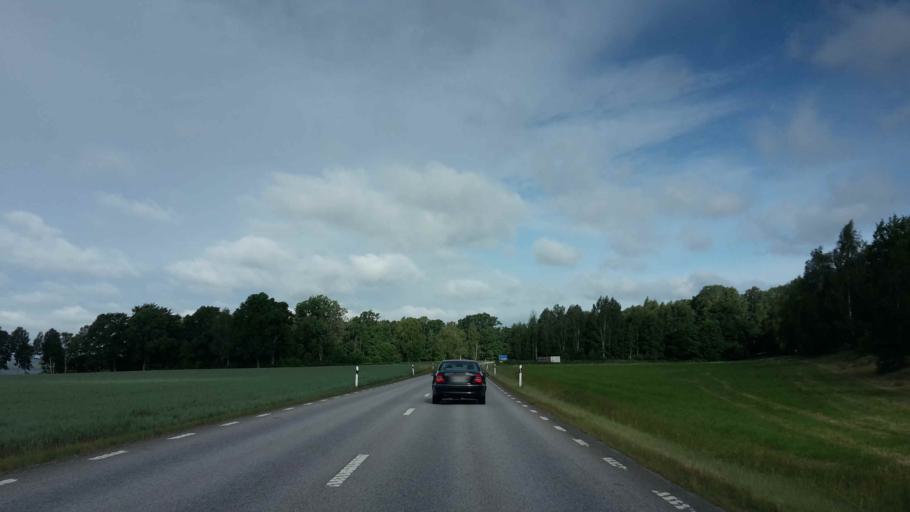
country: SE
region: OEstergoetland
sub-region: Motala Kommun
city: Borensberg
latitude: 58.5730
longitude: 15.2168
